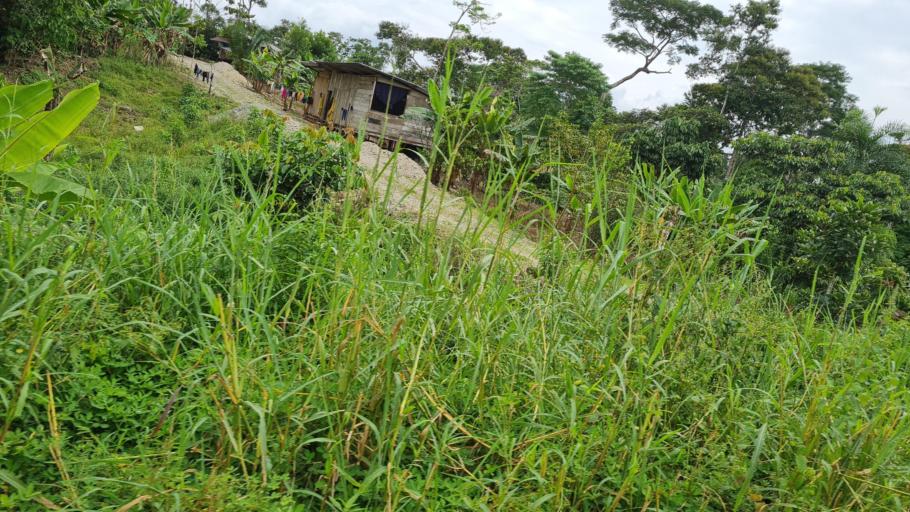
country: EC
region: Napo
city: Tena
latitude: -1.0013
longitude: -77.7634
